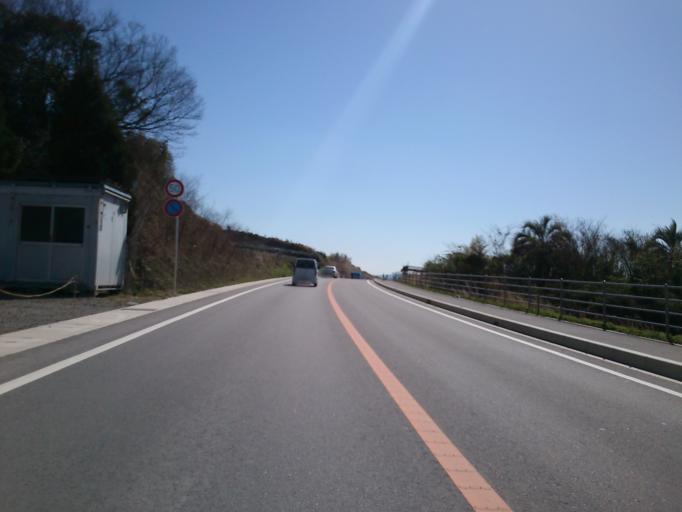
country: JP
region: Kyoto
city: Tanabe
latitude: 34.8276
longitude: 135.8152
